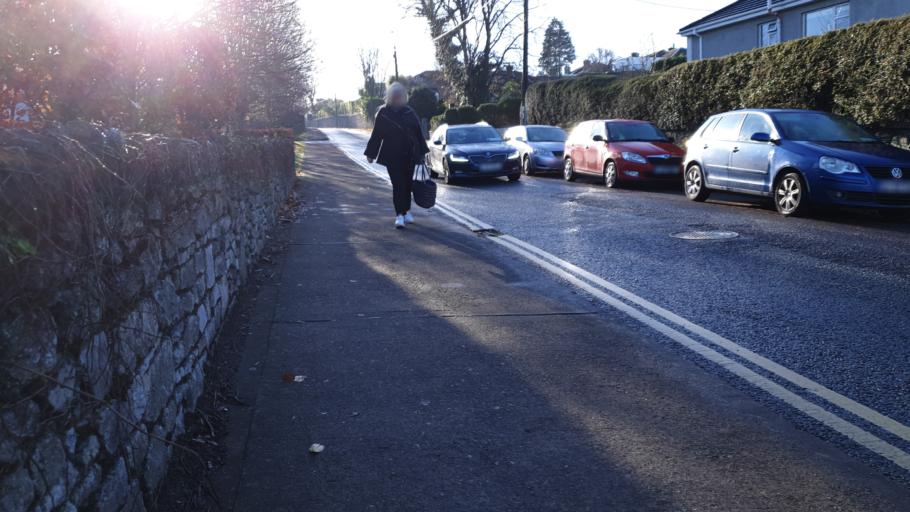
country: IE
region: Munster
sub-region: County Cork
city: Cork
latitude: 51.8941
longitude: -8.4338
